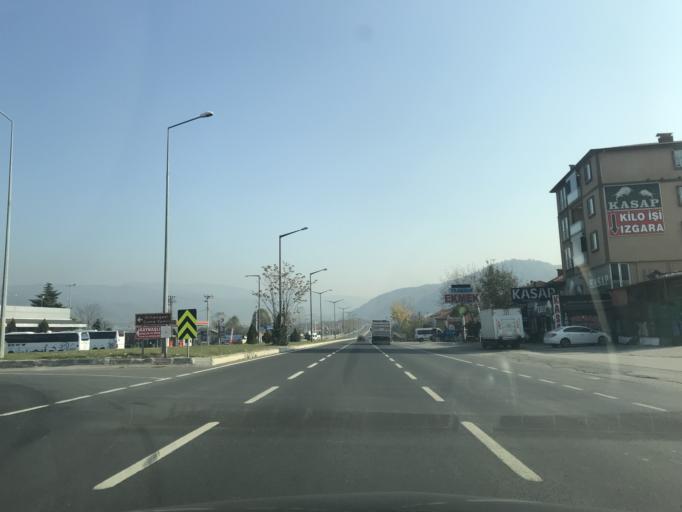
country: TR
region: Duzce
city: Kaynasli
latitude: 40.7757
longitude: 31.3054
